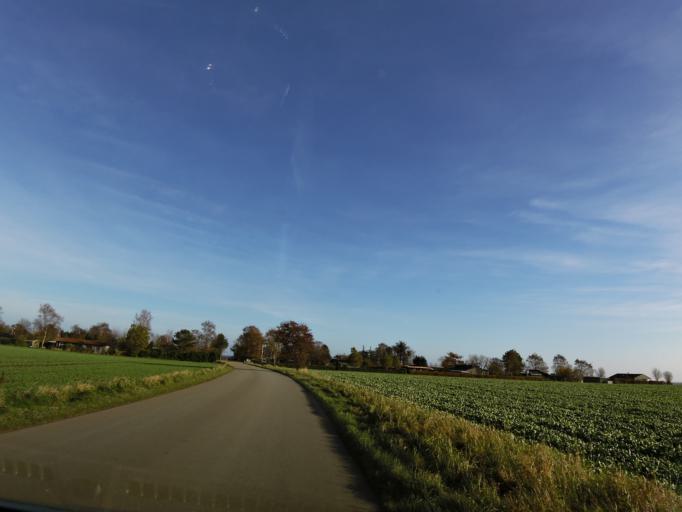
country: DK
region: Central Jutland
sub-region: Arhus Kommune
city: Malling
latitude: 55.9571
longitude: 10.2583
